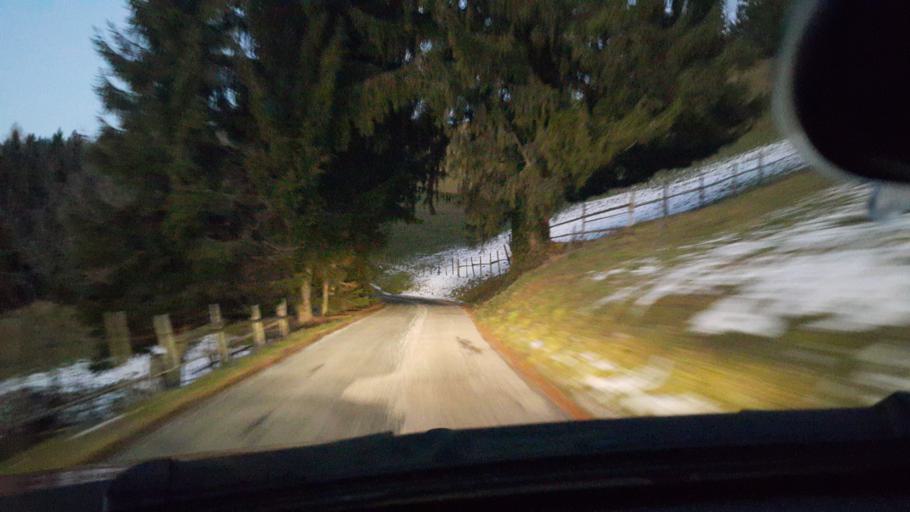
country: AT
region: Styria
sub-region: Politischer Bezirk Graz-Umgebung
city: Stiwoll
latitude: 47.1266
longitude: 15.2213
